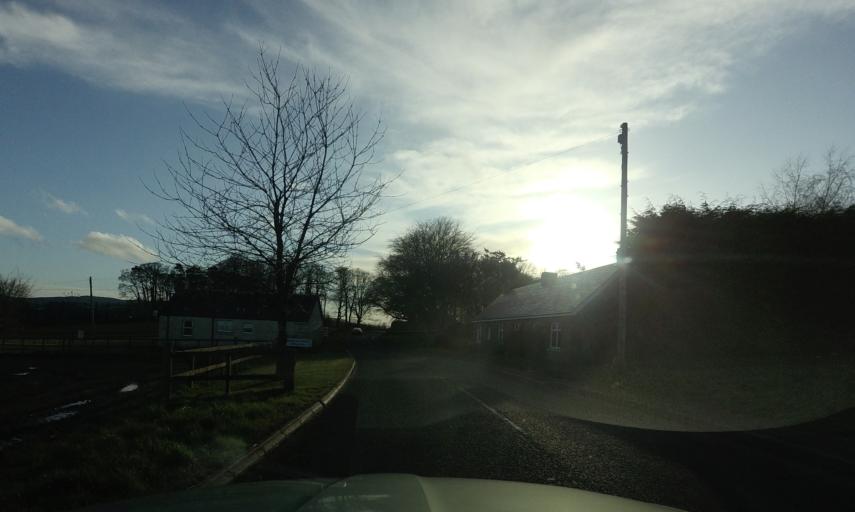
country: GB
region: Scotland
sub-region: Perth and Kinross
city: Errol
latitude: 56.3841
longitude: -3.2326
